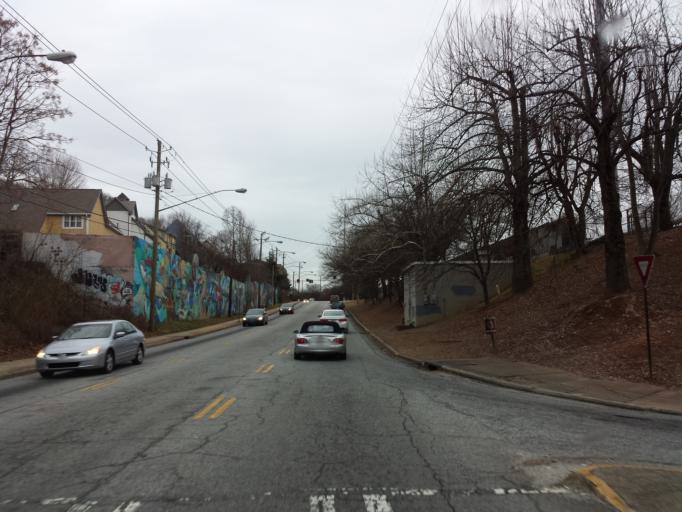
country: US
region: Georgia
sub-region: DeKalb County
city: Druid Hills
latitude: 33.7615
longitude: -84.3309
